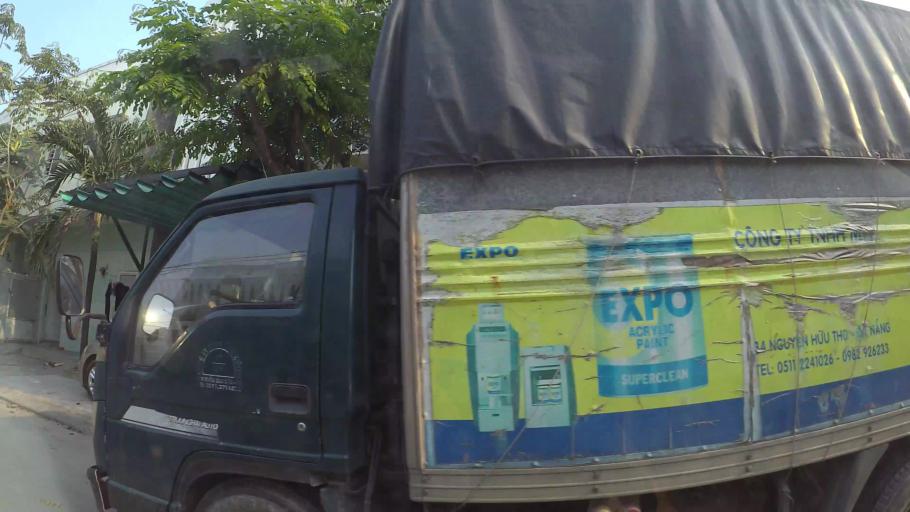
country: VN
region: Da Nang
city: Cam Le
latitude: 16.0222
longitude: 108.2030
